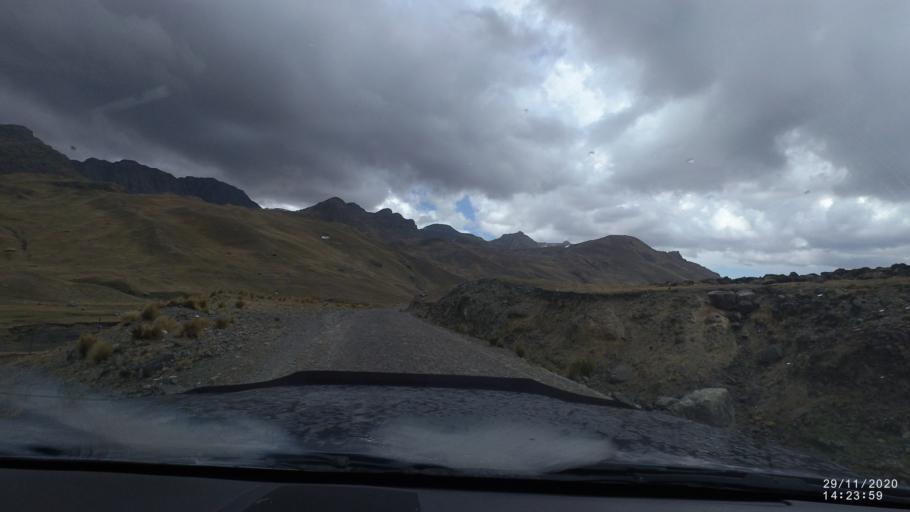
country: BO
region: Cochabamba
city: Sipe Sipe
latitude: -17.2547
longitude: -66.3813
